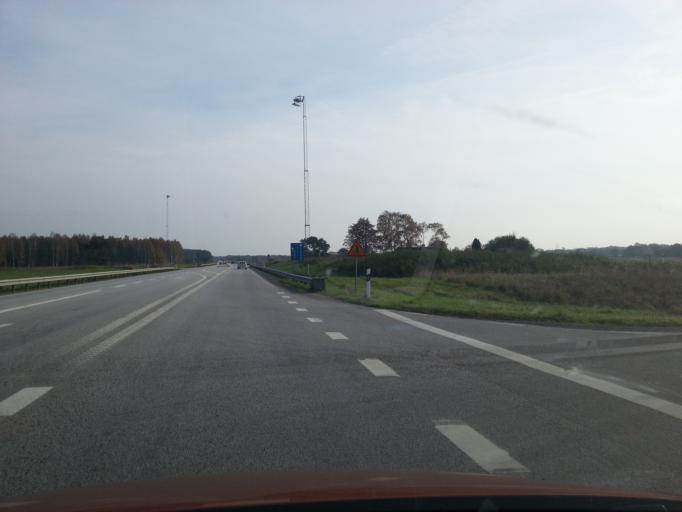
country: SE
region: Skane
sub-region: Lunds Kommun
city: Veberod
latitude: 55.6408
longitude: 13.5409
